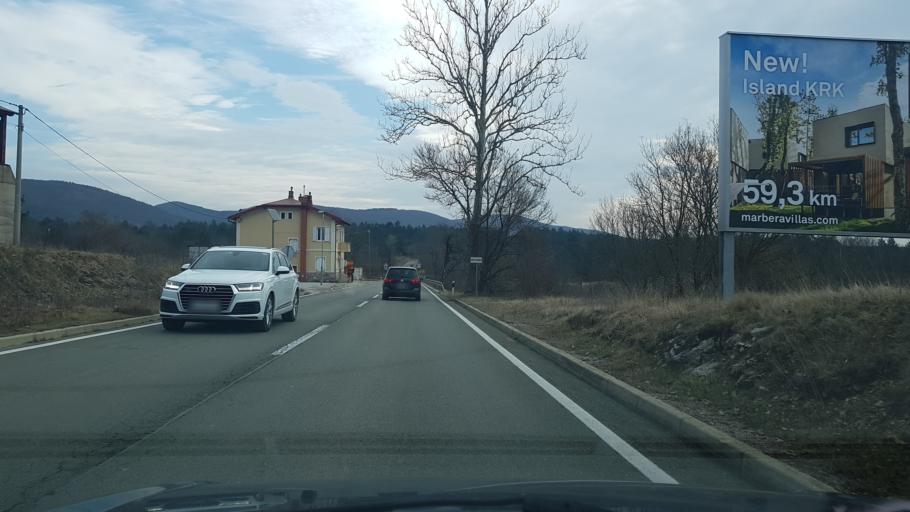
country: SI
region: Ilirska Bistrica
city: Ilirska Bistrica
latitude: 45.4800
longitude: 14.2571
